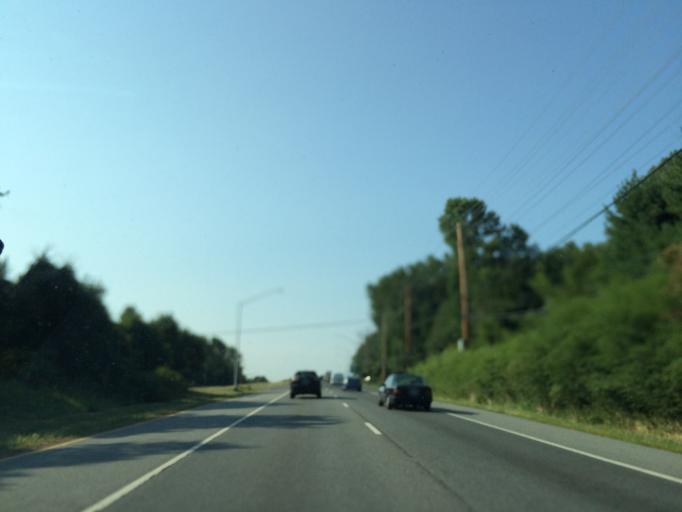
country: US
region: Maryland
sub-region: Prince George's County
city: Bowie
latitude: 38.9723
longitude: -76.7162
